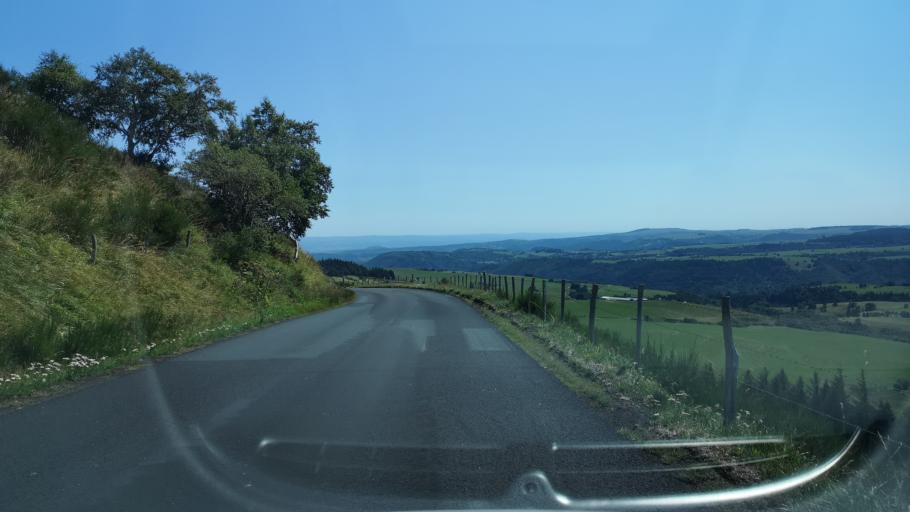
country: FR
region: Auvergne
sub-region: Departement du Puy-de-Dome
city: Mont-Dore
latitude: 45.5901
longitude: 2.8673
